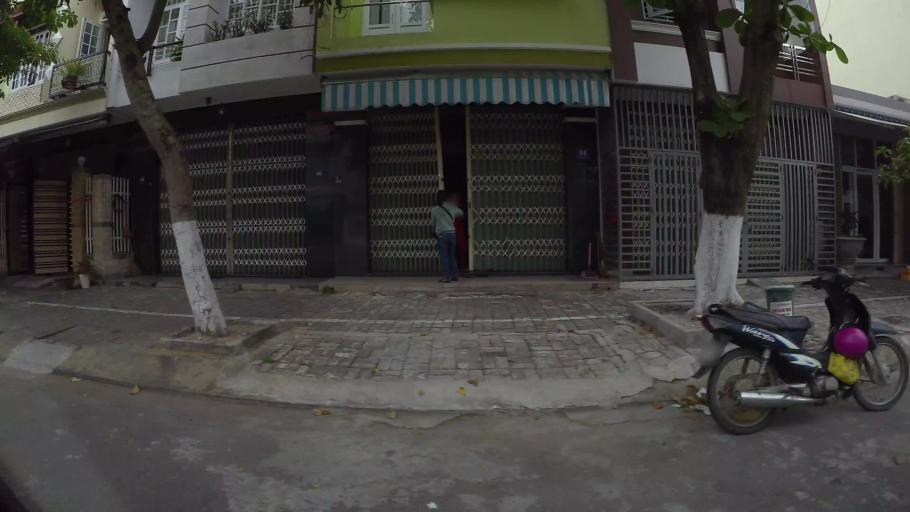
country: VN
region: Da Nang
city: Cam Le
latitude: 16.0245
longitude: 108.2119
